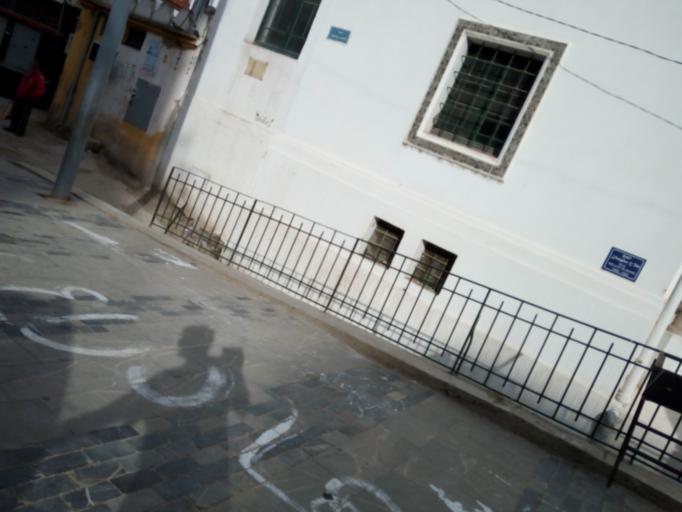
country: DZ
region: Constantine
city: Constantine
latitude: 36.3664
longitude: 6.6141
